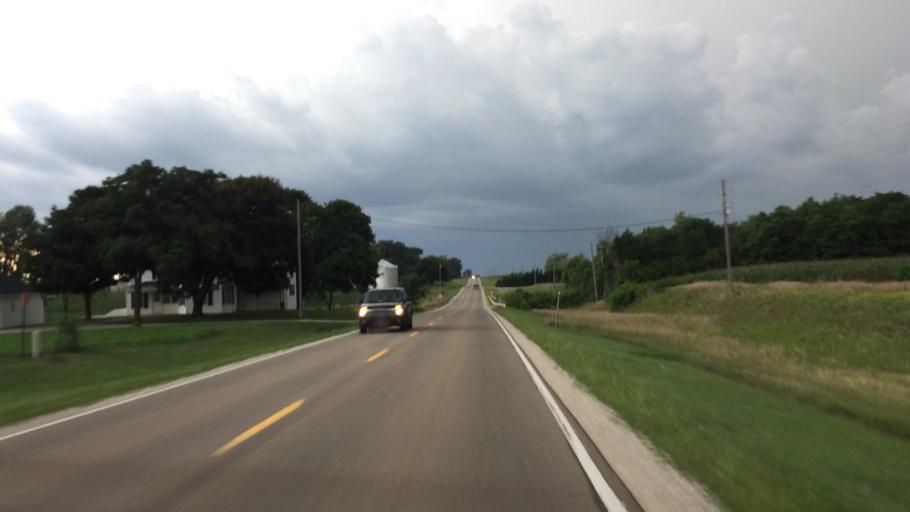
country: US
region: Iowa
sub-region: Henry County
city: New London
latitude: 40.7732
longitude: -91.4554
